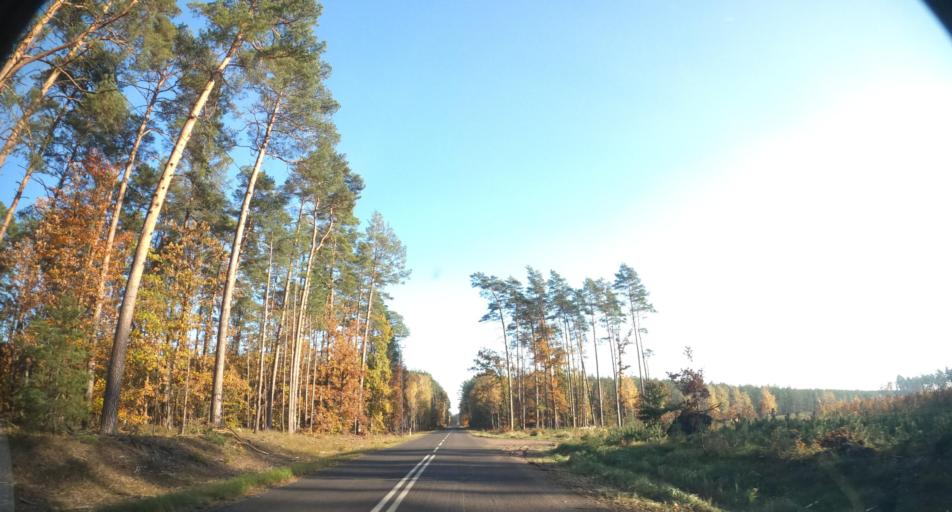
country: PL
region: West Pomeranian Voivodeship
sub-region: Powiat policki
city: Nowe Warpno
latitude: 53.6036
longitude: 14.3230
